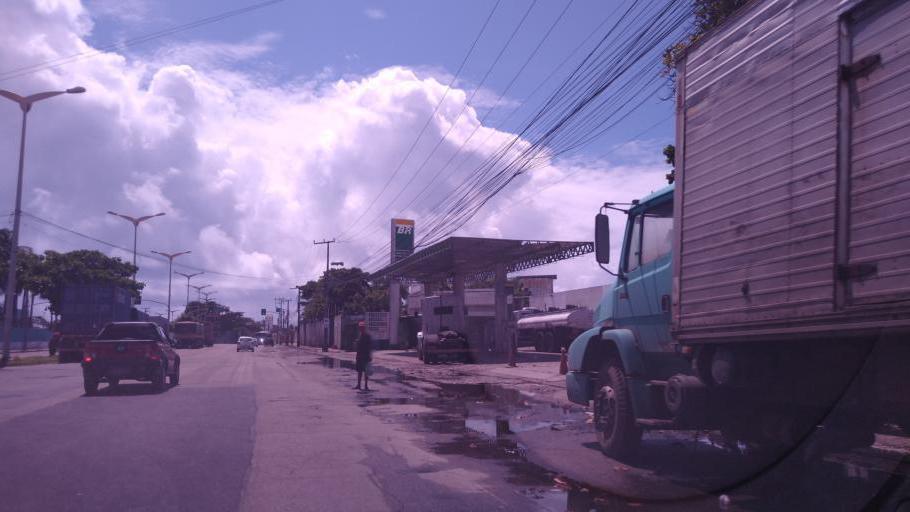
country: BR
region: Ceara
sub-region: Fortaleza
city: Fortaleza
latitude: -3.7154
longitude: -38.4742
